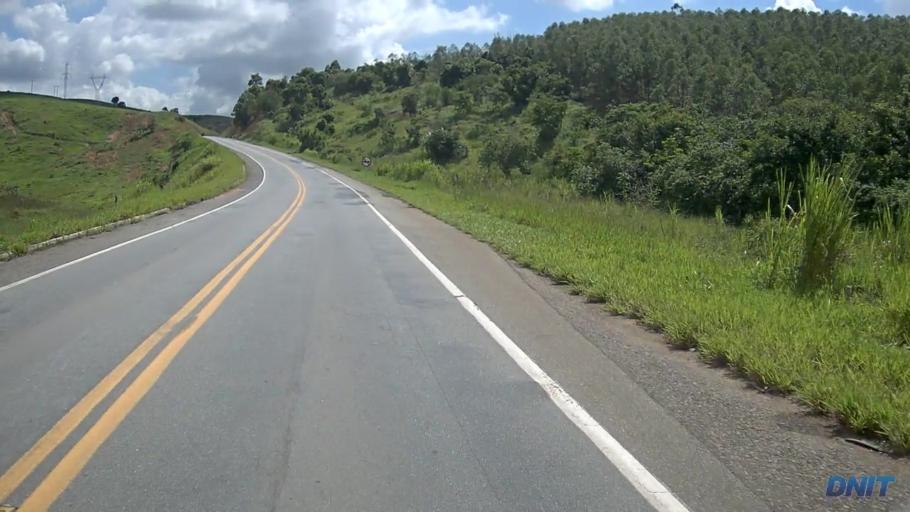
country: BR
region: Minas Gerais
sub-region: Belo Oriente
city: Belo Oriente
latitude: -19.1006
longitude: -42.1988
